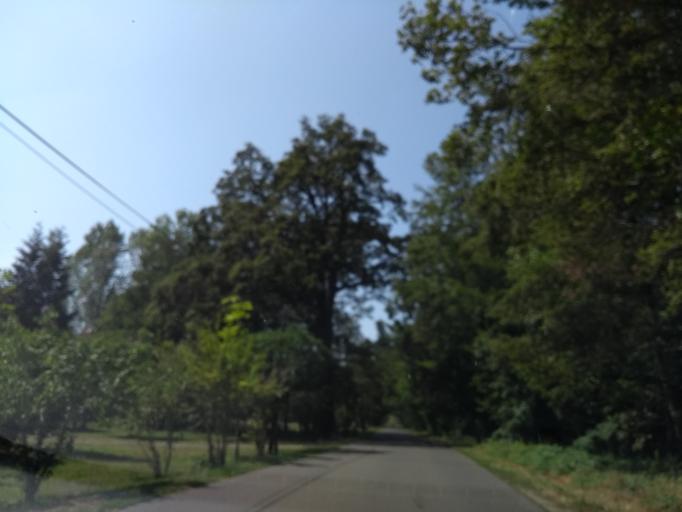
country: DE
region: Brandenburg
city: Burg
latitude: 51.8516
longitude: 14.1207
